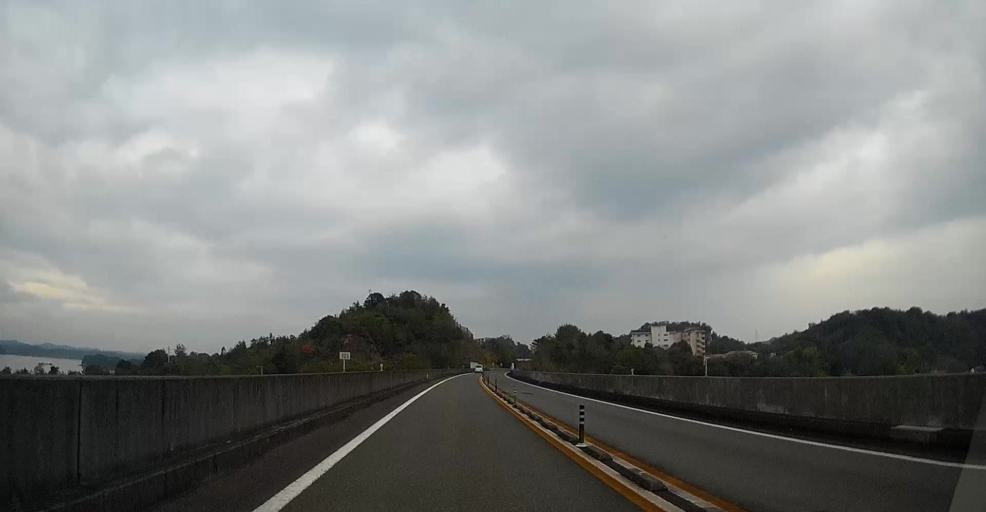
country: JP
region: Kumamoto
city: Yatsushiro
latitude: 32.5192
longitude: 130.4162
